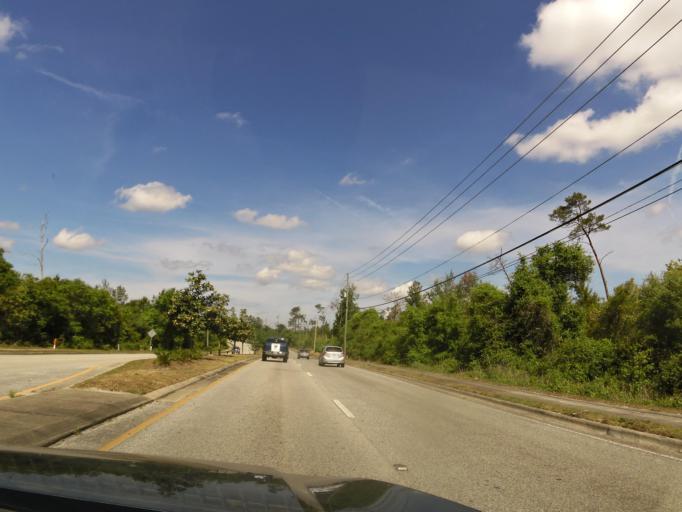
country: US
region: Florida
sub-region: Volusia County
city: Lake Helen
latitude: 28.9458
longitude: -81.2280
